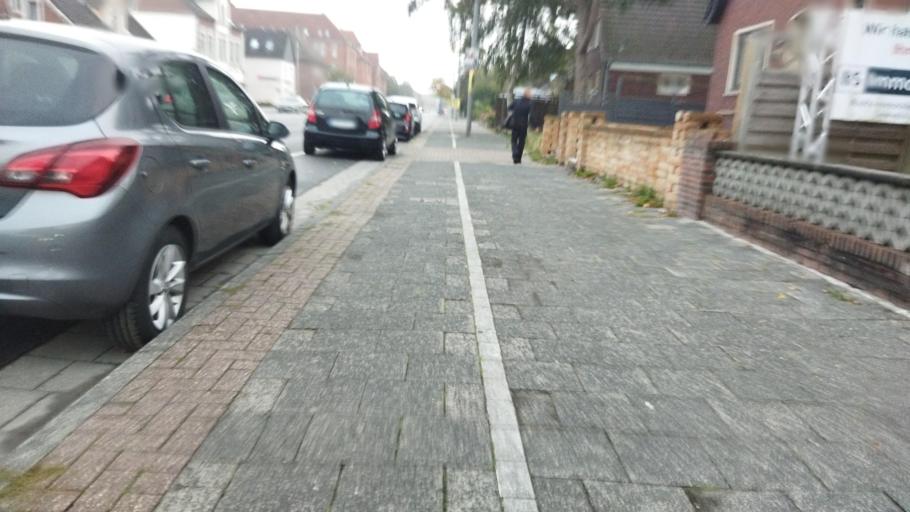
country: DE
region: Lower Saxony
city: Emden
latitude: 53.3841
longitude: 7.2075
